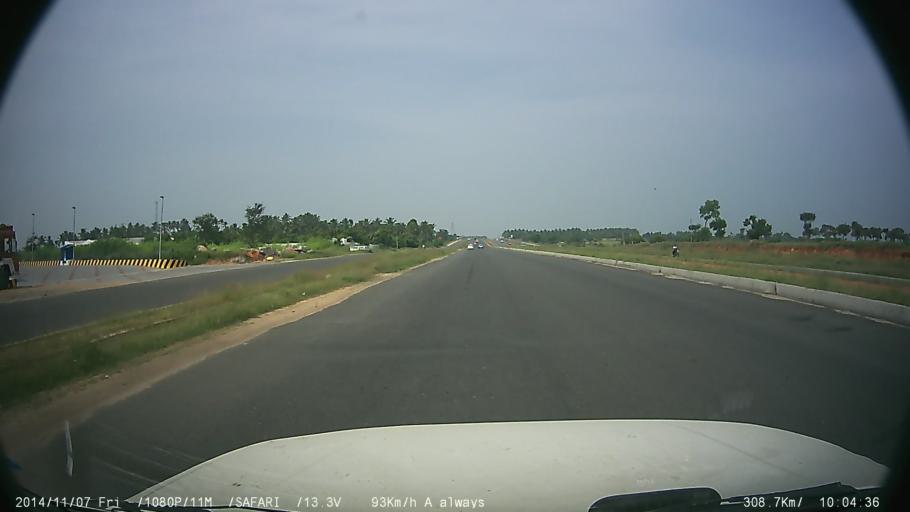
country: IN
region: Tamil Nadu
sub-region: Tiruppur
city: Uttukkuli
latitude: 11.2065
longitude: 77.3831
